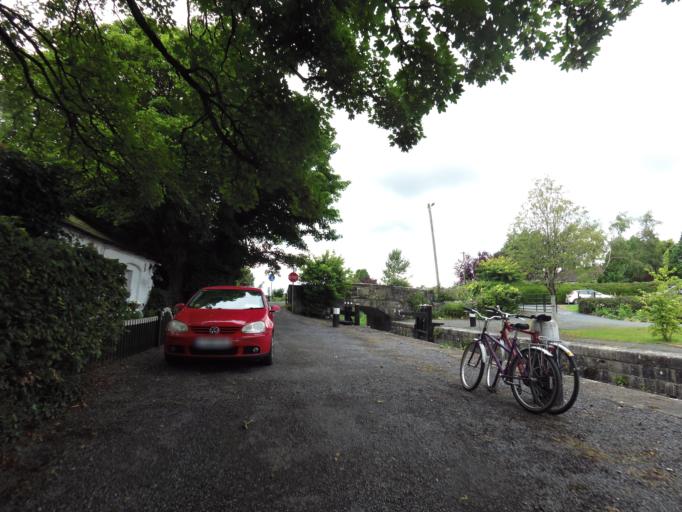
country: IE
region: Leinster
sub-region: An Iarmhi
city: An Muileann gCearr
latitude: 53.5346
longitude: -7.4679
